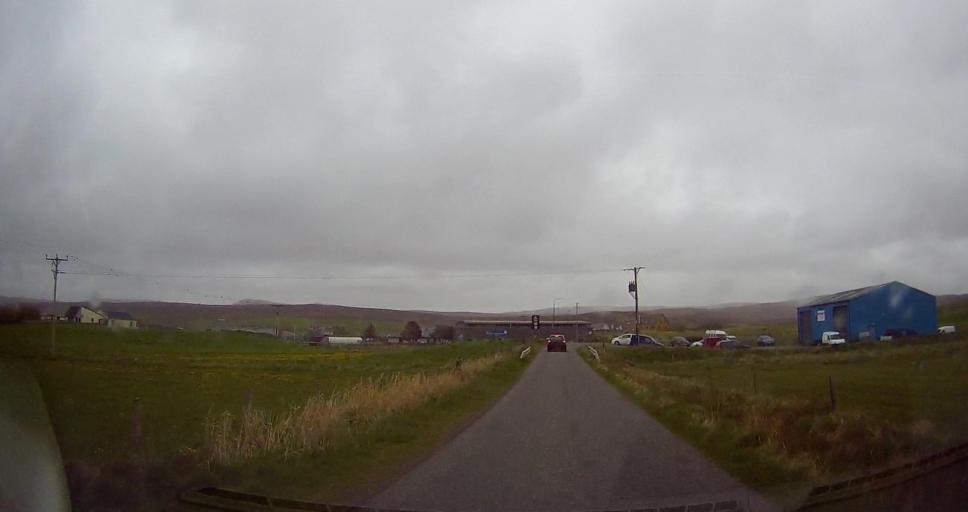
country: GB
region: Scotland
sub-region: Shetland Islands
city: Lerwick
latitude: 60.2841
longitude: -1.3826
